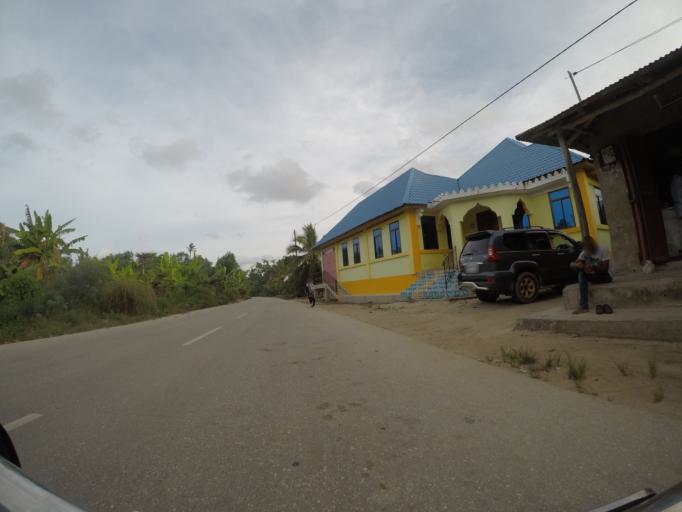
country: TZ
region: Pemba South
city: Mtambile
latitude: -5.3884
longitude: 39.7470
